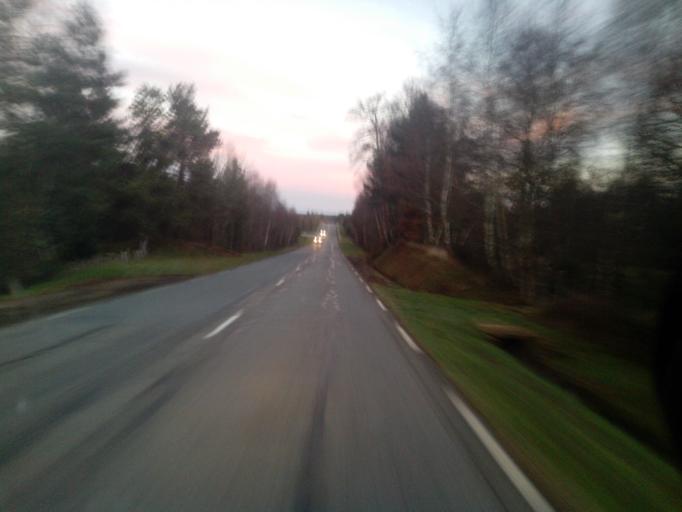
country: FR
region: Limousin
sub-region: Departement de la Correze
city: Meymac
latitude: 45.5094
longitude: 2.1970
